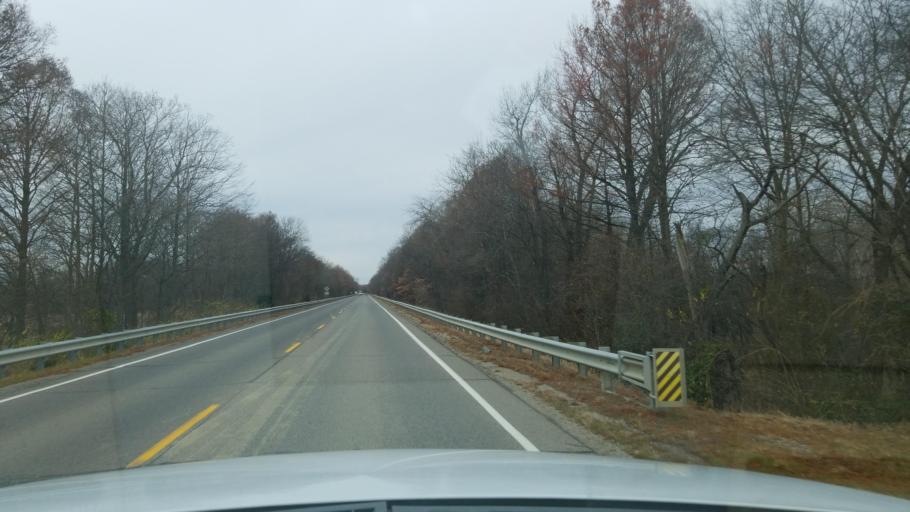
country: US
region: Indiana
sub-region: Posey County
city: Mount Vernon
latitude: 37.9336
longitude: -88.0058
